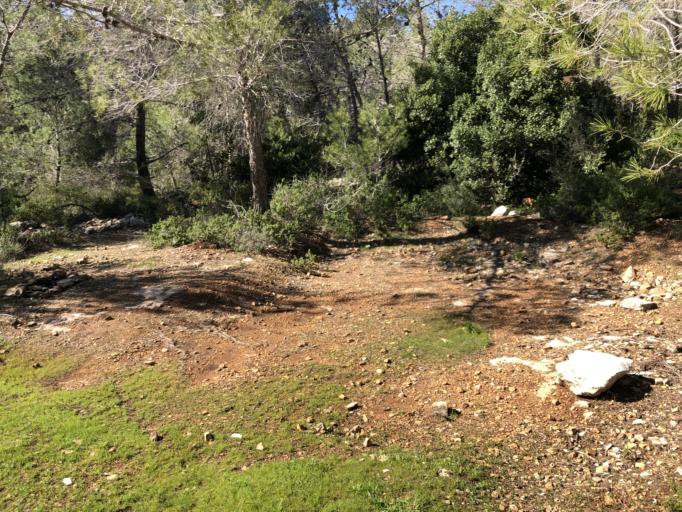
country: IL
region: Jerusalem
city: Bet Shemesh
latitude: 31.7465
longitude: 35.0462
